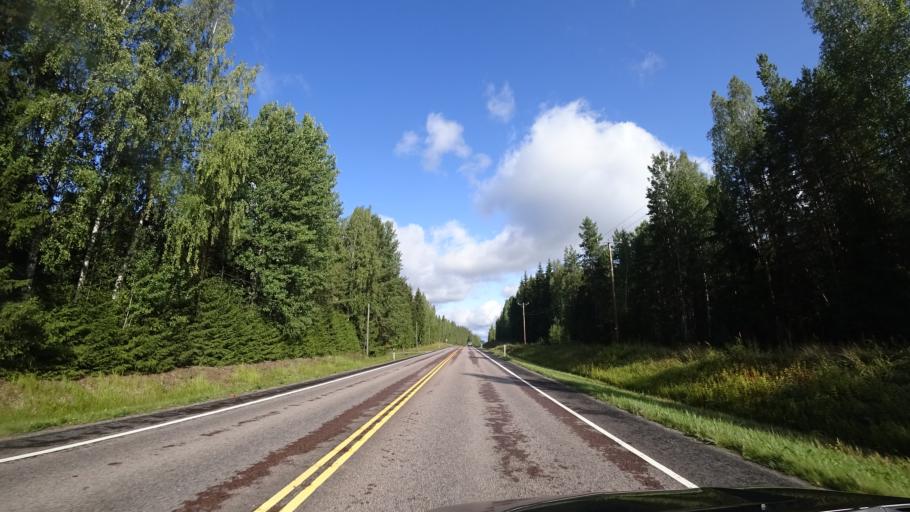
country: FI
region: Uusimaa
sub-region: Helsinki
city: Nurmijaervi
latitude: 60.5058
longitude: 24.9306
